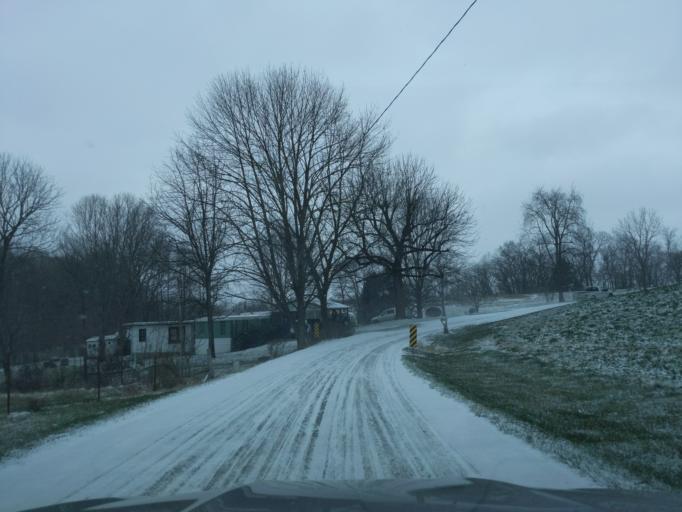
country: US
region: Indiana
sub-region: Decatur County
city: Westport
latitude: 39.2285
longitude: -85.5115
